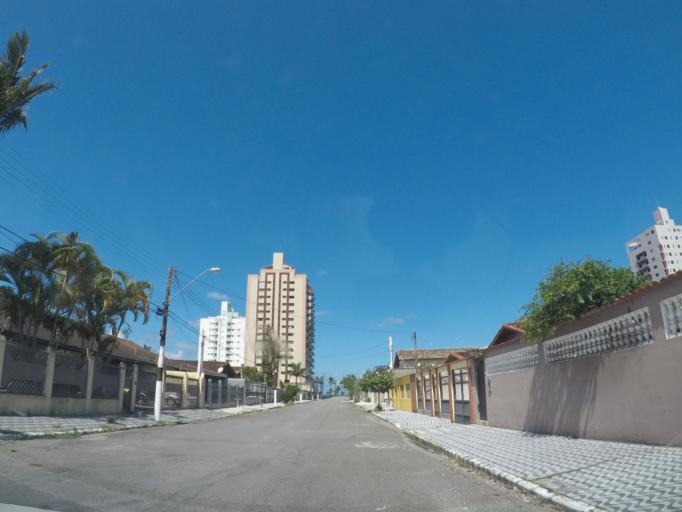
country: BR
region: Sao Paulo
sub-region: Mongagua
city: Mongagua
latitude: -24.0686
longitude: -46.5672
